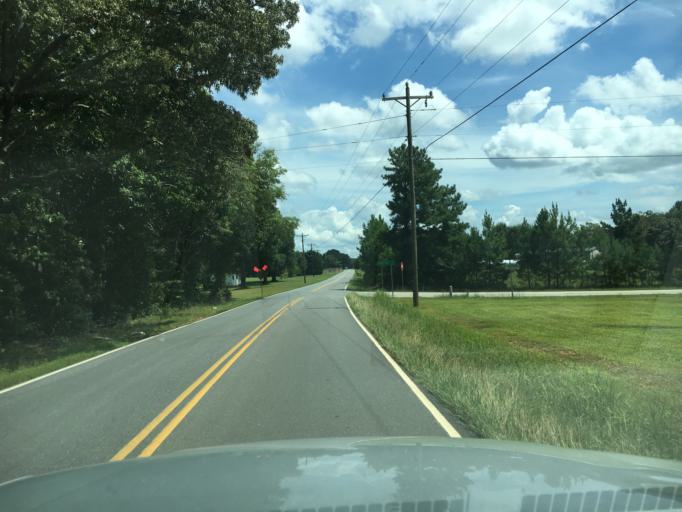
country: US
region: South Carolina
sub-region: Anderson County
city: Belton
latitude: 34.5481
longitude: -82.4585
